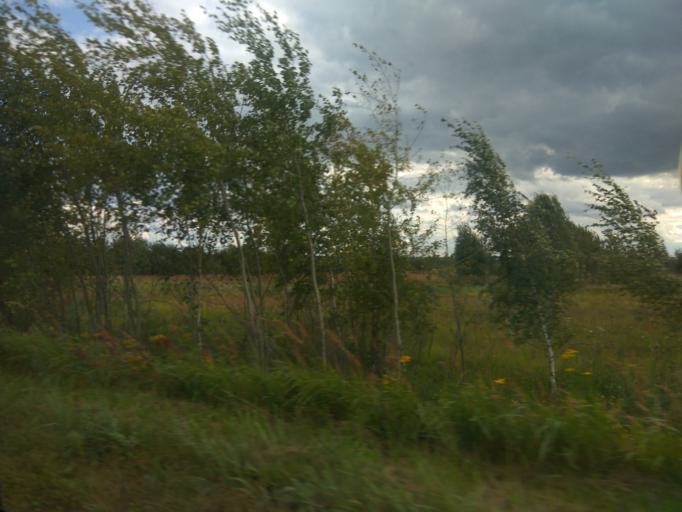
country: RU
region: Moskovskaya
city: Bronnitsy
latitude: 55.4549
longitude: 38.2560
